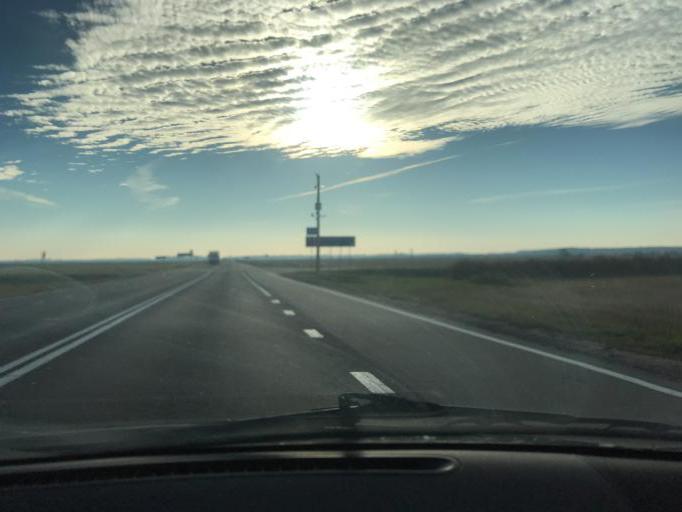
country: BY
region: Brest
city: Drahichyn
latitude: 52.2192
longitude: 25.1720
